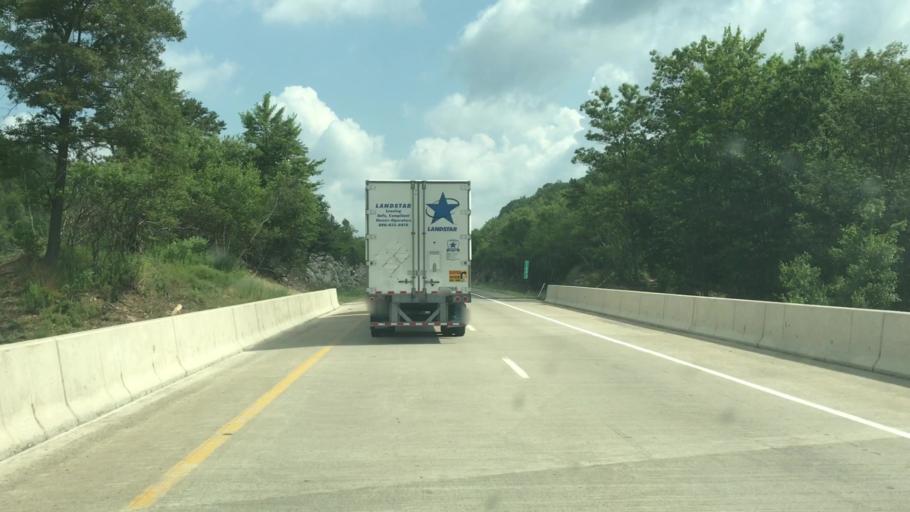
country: US
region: Pennsylvania
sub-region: Schuylkill County
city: Hometown
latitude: 40.8410
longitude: -76.0594
